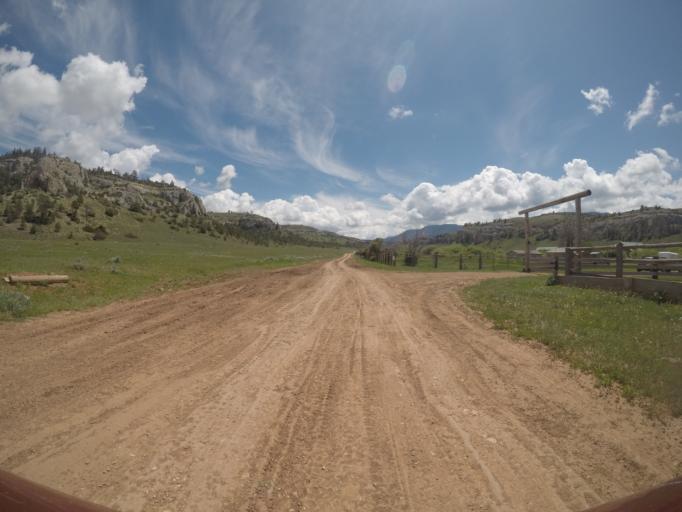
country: US
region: Montana
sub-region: Yellowstone County
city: Laurel
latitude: 45.2391
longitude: -108.6314
